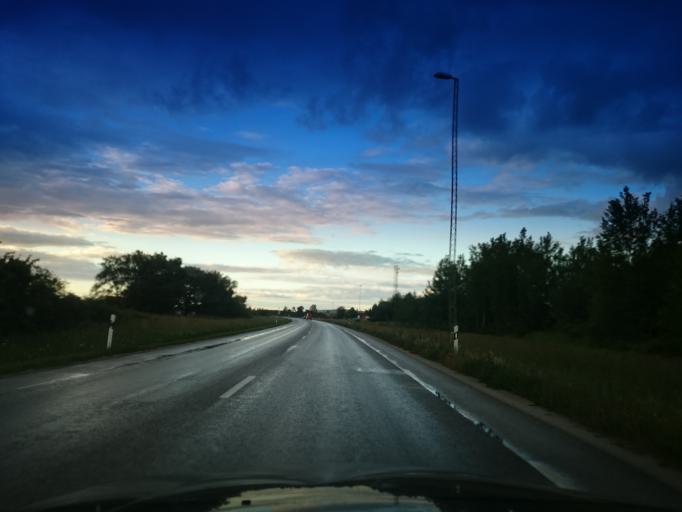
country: SE
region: Gotland
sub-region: Gotland
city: Visby
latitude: 57.6341
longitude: 18.3297
